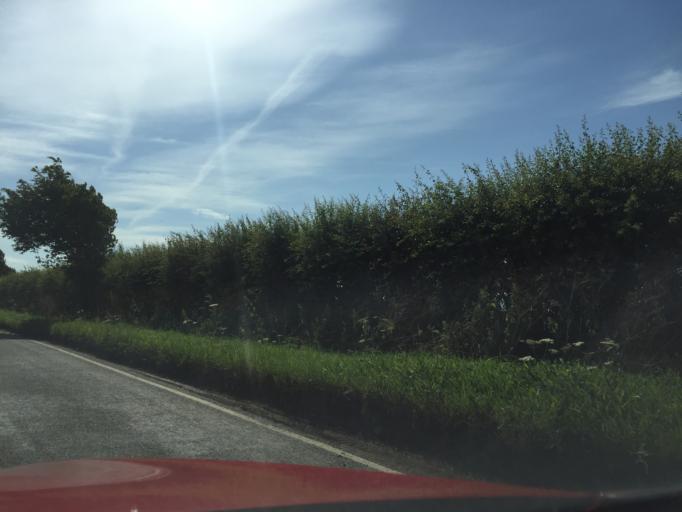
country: GB
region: England
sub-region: Gloucestershire
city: Stonehouse
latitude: 51.7963
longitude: -2.3373
